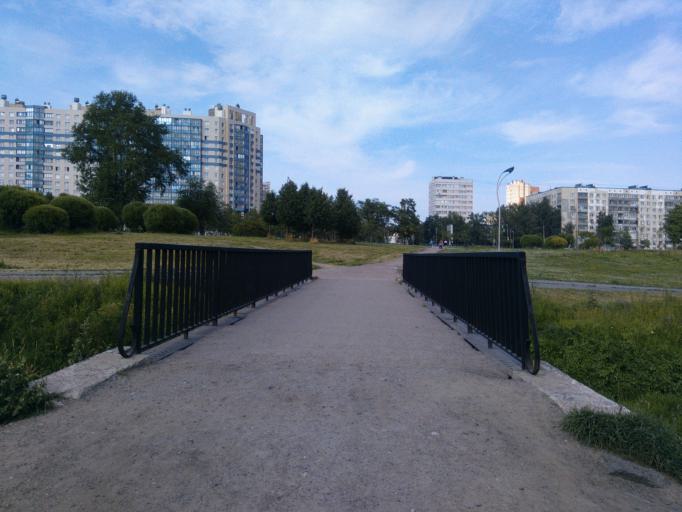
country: RU
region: St.-Petersburg
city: Grazhdanka
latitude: 60.0263
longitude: 30.4013
